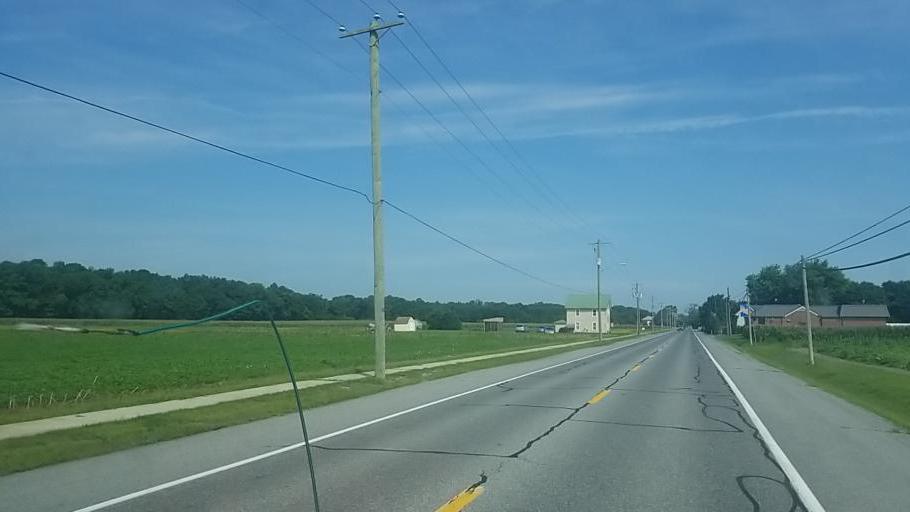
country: US
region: Delaware
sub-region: Sussex County
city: Millsboro
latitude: 38.5401
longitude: -75.2383
